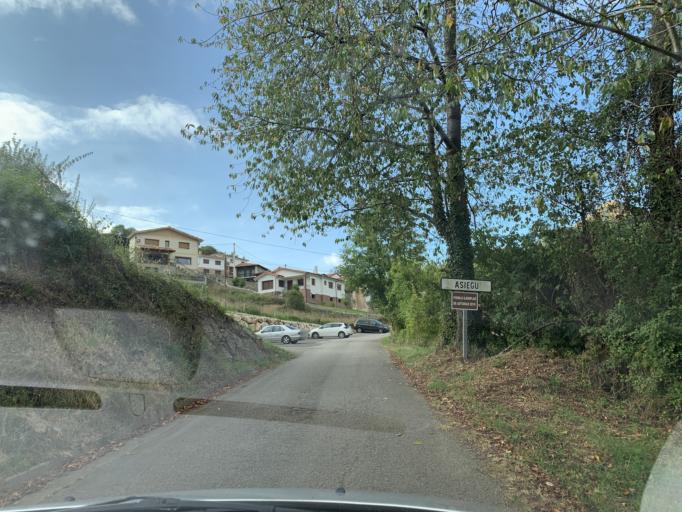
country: ES
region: Asturias
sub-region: Province of Asturias
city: Carrena
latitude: 43.3241
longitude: -4.8630
